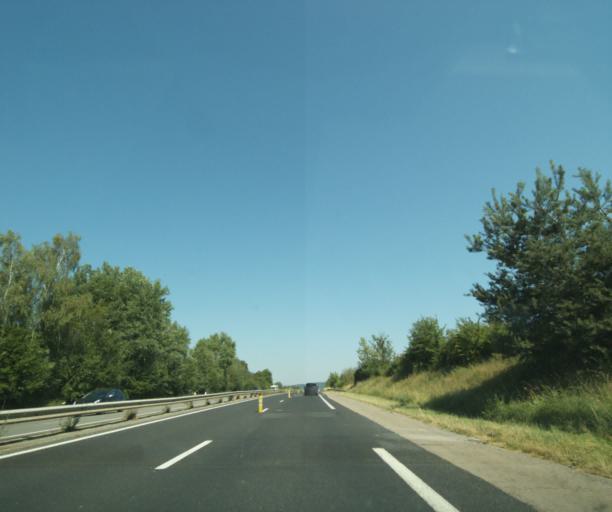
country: FR
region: Lorraine
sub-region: Departement de Meurthe-et-Moselle
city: Domgermain
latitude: 48.6571
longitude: 5.8403
